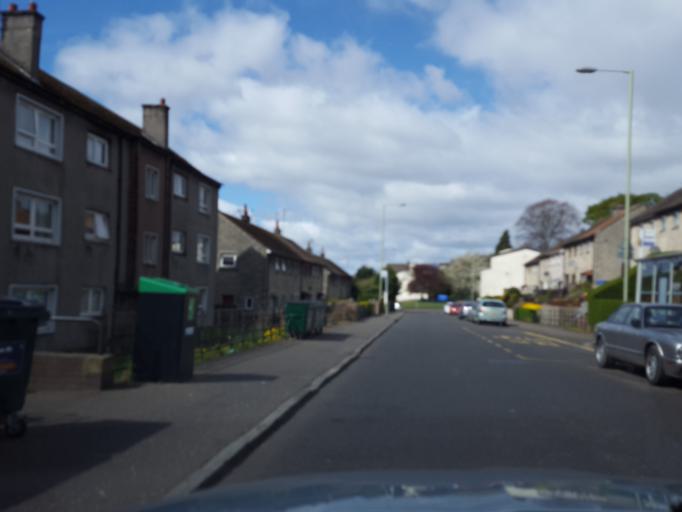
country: GB
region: Scotland
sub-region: Angus
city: Muirhead
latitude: 56.4757
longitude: -3.0331
